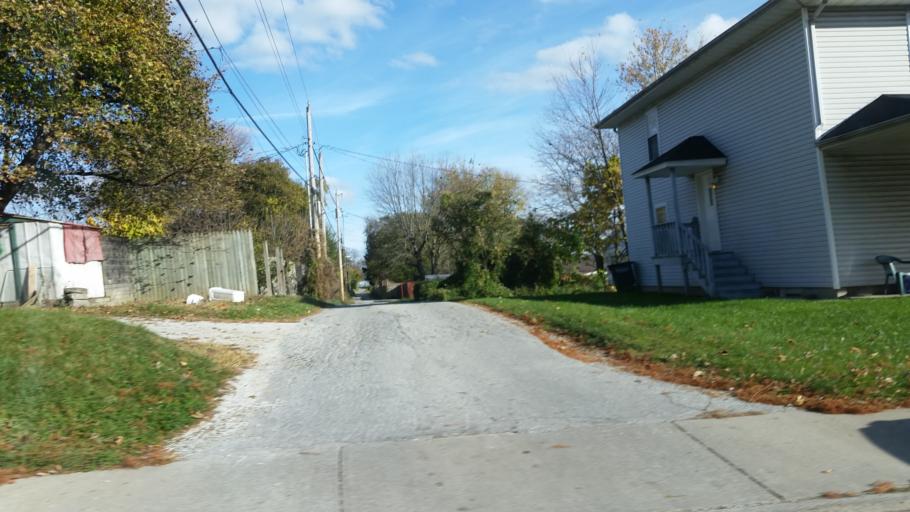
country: US
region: Indiana
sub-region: Howard County
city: Kokomo
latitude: 40.4889
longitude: -86.1174
